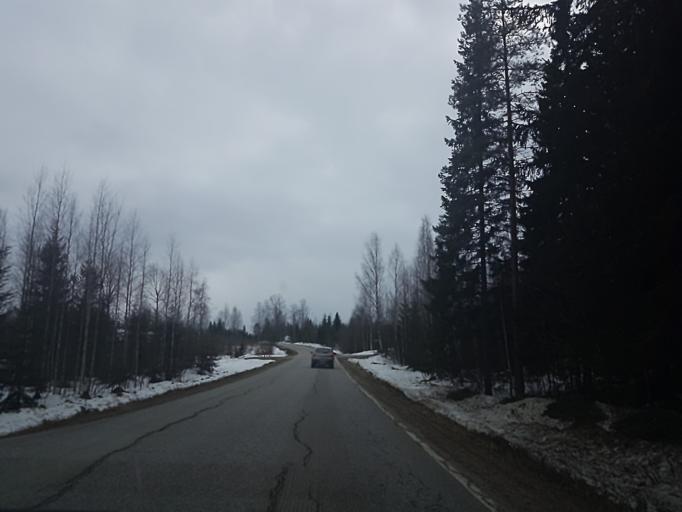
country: FI
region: Northern Savo
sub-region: Koillis-Savo
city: Kaavi
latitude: 62.9992
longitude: 28.5029
